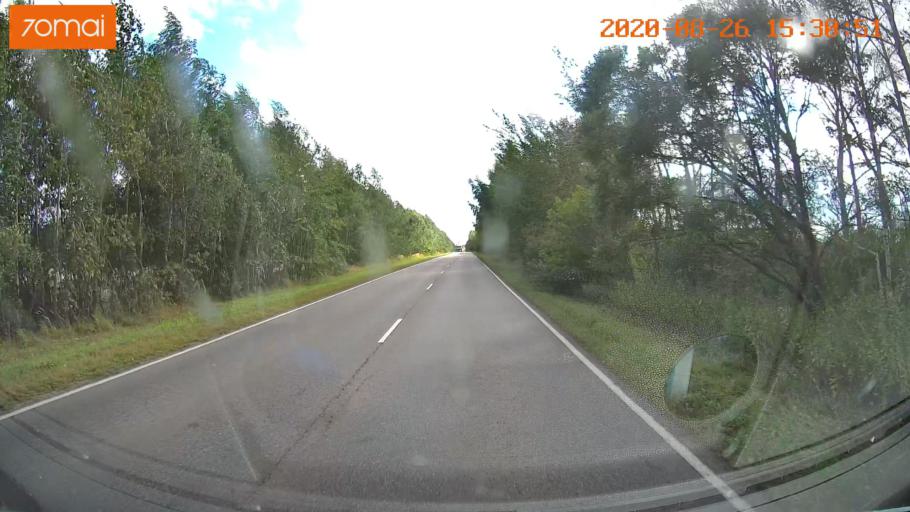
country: RU
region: Tula
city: Severo-Zadonsk
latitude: 54.0866
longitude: 38.3932
